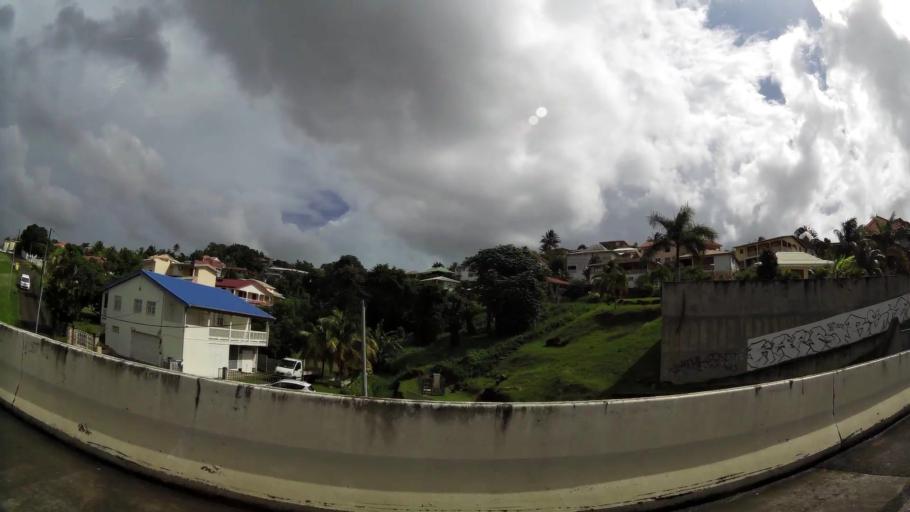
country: MQ
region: Martinique
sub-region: Martinique
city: Ducos
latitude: 14.5751
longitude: -60.9852
